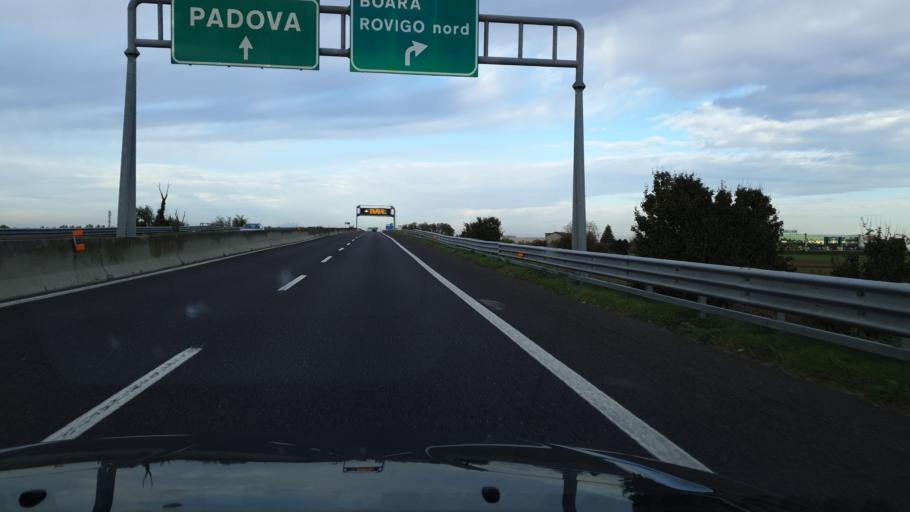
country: IT
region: Veneto
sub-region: Provincia di Padova
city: Boara Pisani
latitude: 45.1093
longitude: 11.7604
